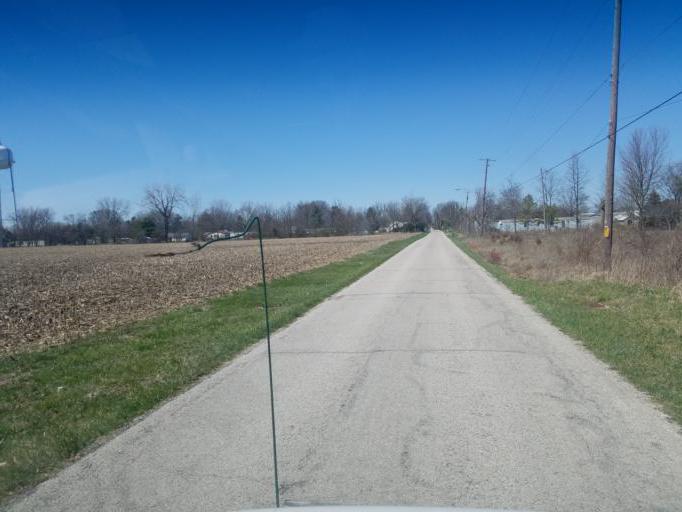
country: US
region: Ohio
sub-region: Morrow County
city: Cardington
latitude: 40.4944
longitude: -82.9019
